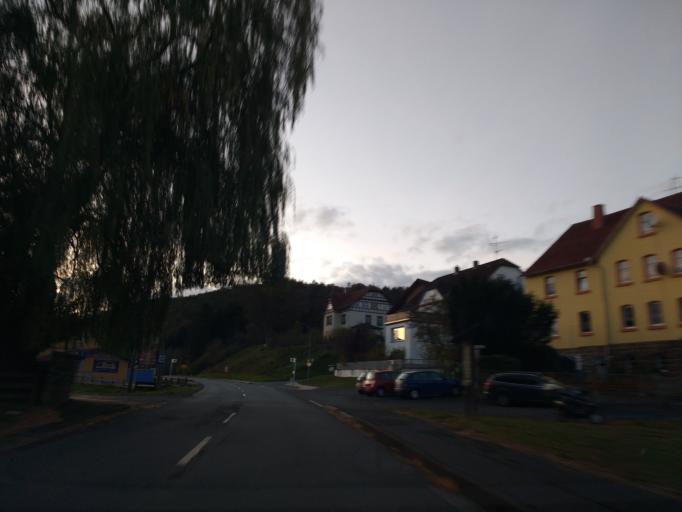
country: DE
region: Hesse
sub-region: Regierungsbezirk Kassel
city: Waldeck
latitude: 51.1686
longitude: 9.0810
